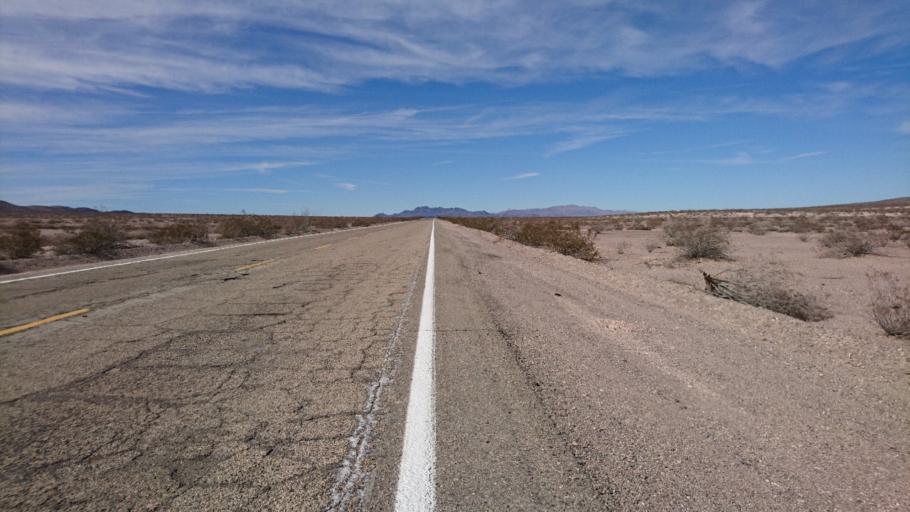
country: US
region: California
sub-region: San Bernardino County
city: Twentynine Palms
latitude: 34.7046
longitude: -116.0750
